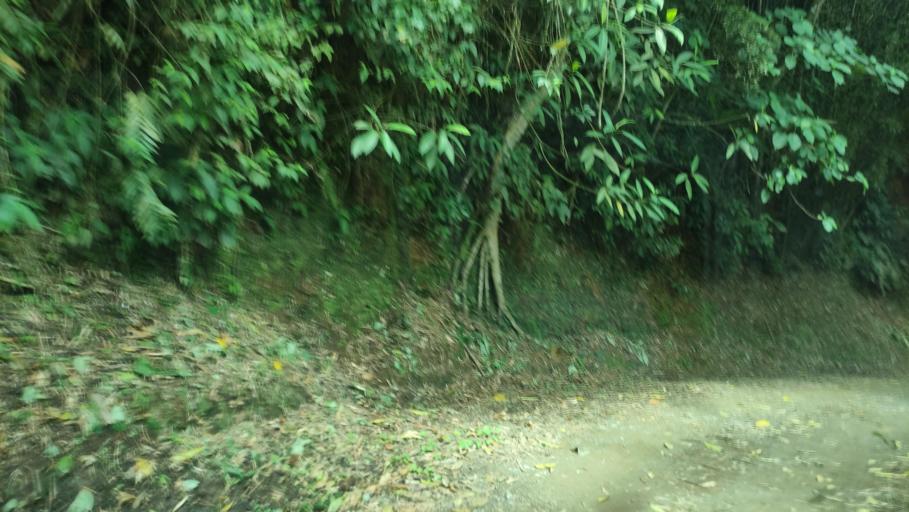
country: CO
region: Caldas
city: Palestina
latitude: 5.0715
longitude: -75.5875
